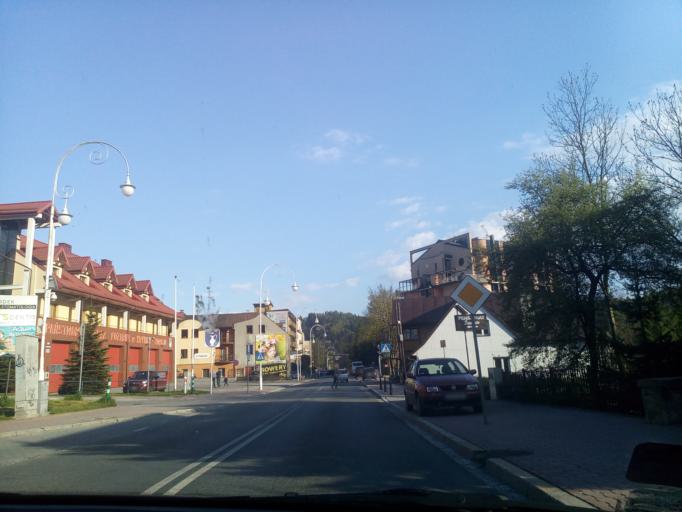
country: PL
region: Lesser Poland Voivodeship
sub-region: Powiat nowosadecki
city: Krynica-Zdroj
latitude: 49.4268
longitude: 20.9542
